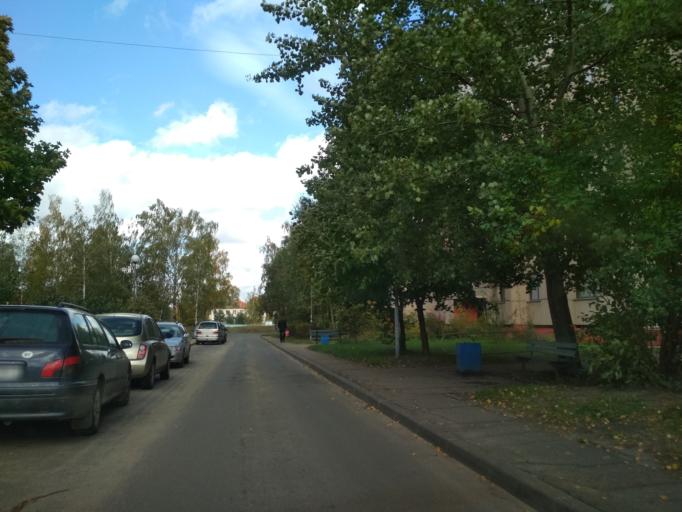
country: BY
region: Minsk
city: Mar''ina Horka
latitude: 53.5040
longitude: 28.1603
